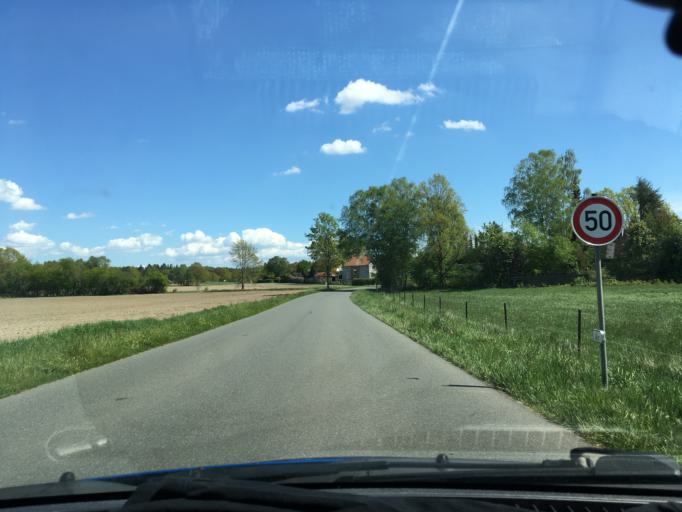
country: DE
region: Lower Saxony
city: Stoetze
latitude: 53.0683
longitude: 10.7853
